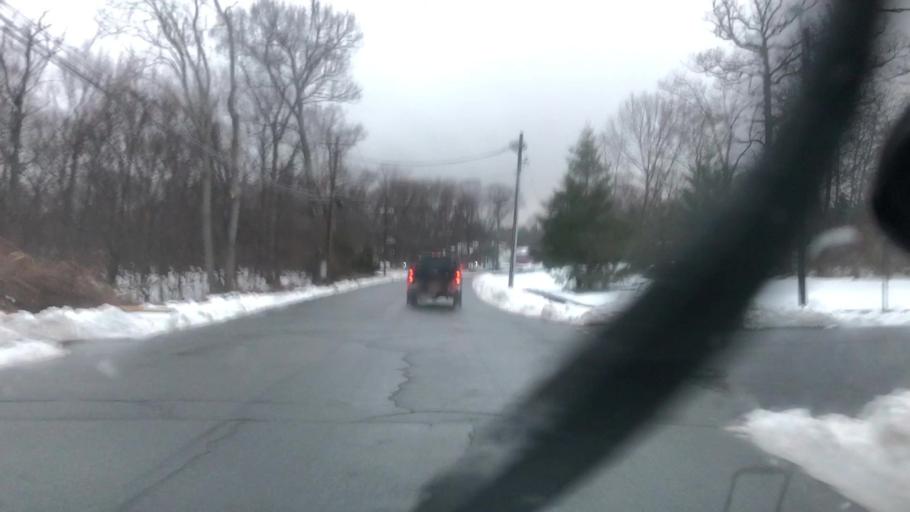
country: US
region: New Jersey
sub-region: Somerset County
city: Somerset
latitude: 40.5185
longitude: -74.5021
